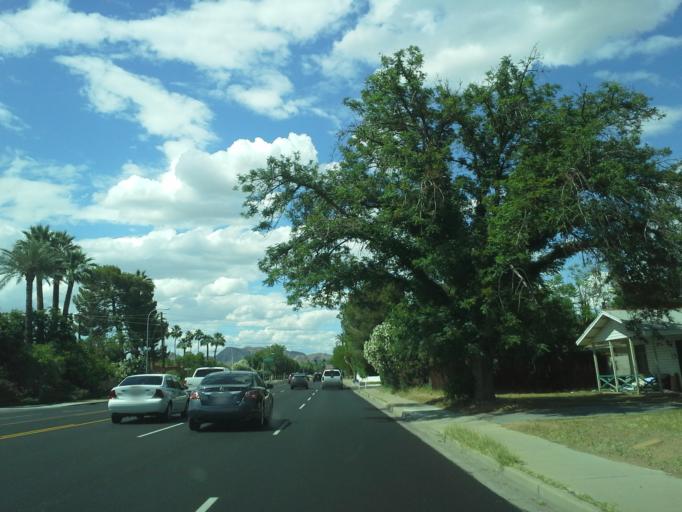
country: US
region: Arizona
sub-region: Maricopa County
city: Paradise Valley
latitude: 33.4900
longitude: -111.9868
